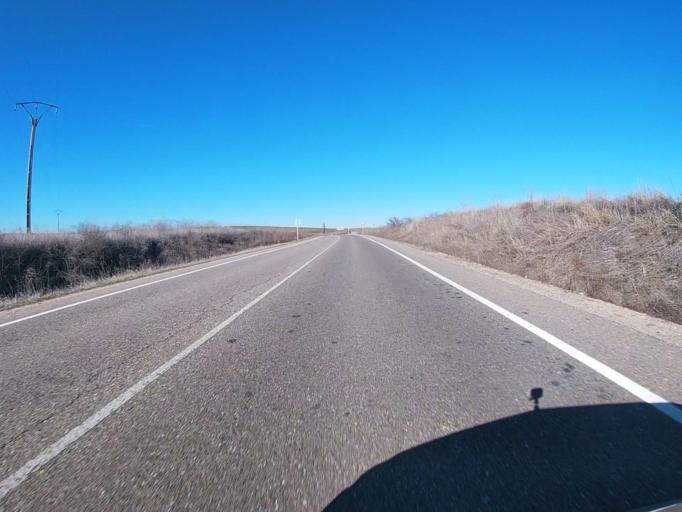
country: ES
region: Castille and Leon
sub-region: Provincia de Salamanca
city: Almenara de Tormes
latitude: 41.0660
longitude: -5.8253
